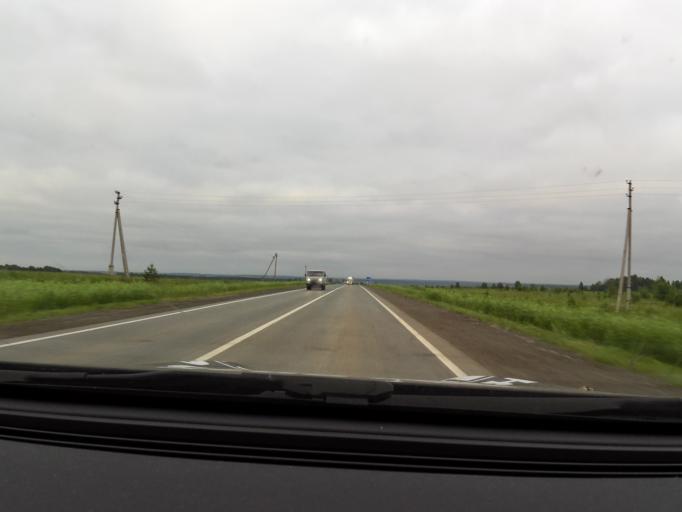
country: RU
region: Perm
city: Karagay
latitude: 58.2814
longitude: 54.8418
